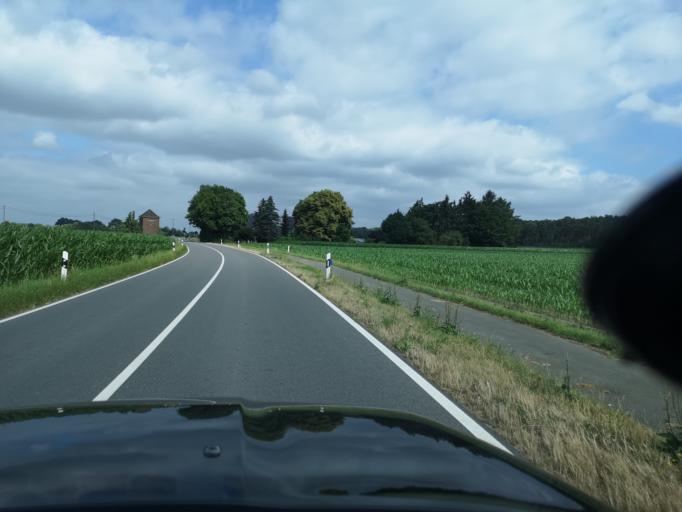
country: DE
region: North Rhine-Westphalia
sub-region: Regierungsbezirk Dusseldorf
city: Hamminkeln
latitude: 51.7388
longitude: 6.6479
